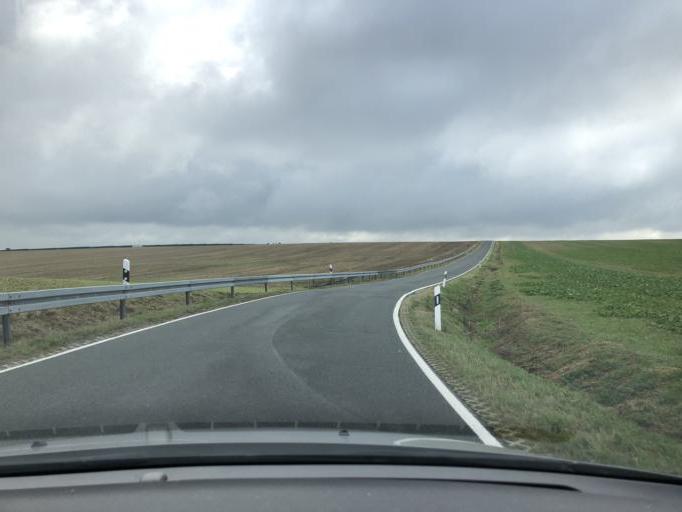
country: DE
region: Thuringia
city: Wachstedt
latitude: 51.3049
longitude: 10.2386
